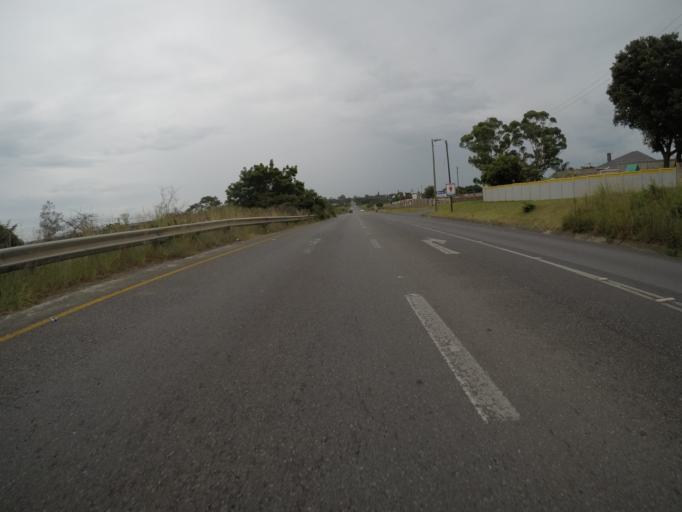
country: ZA
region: Eastern Cape
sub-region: Buffalo City Metropolitan Municipality
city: East London
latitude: -32.9681
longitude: 27.8466
